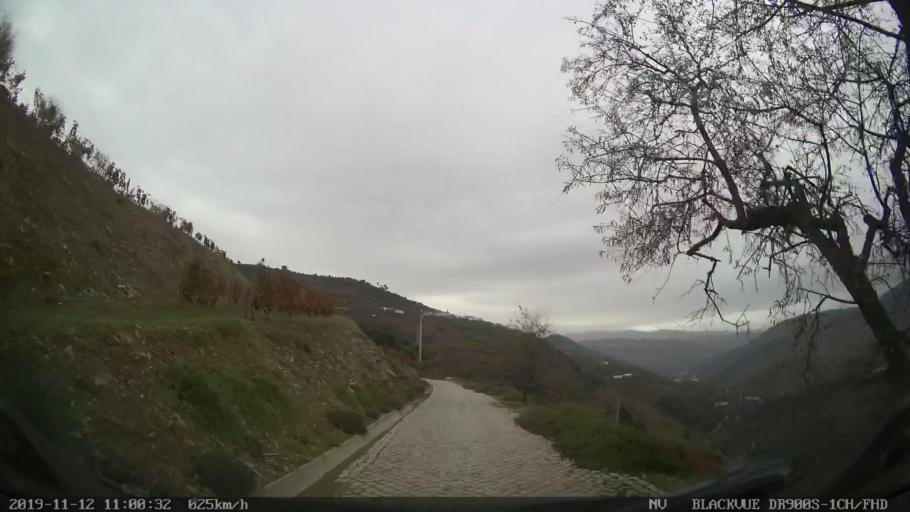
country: PT
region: Vila Real
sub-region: Sabrosa
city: Vilela
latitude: 41.2091
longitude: -7.5347
